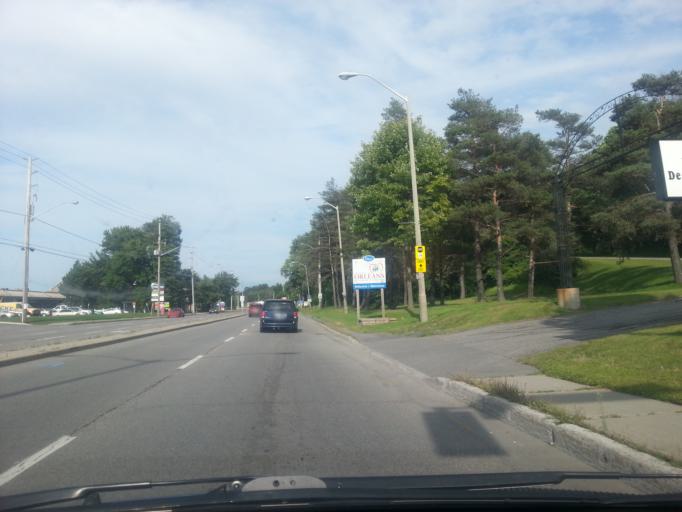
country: CA
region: Quebec
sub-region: Outaouais
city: Gatineau
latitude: 45.4613
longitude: -75.5490
